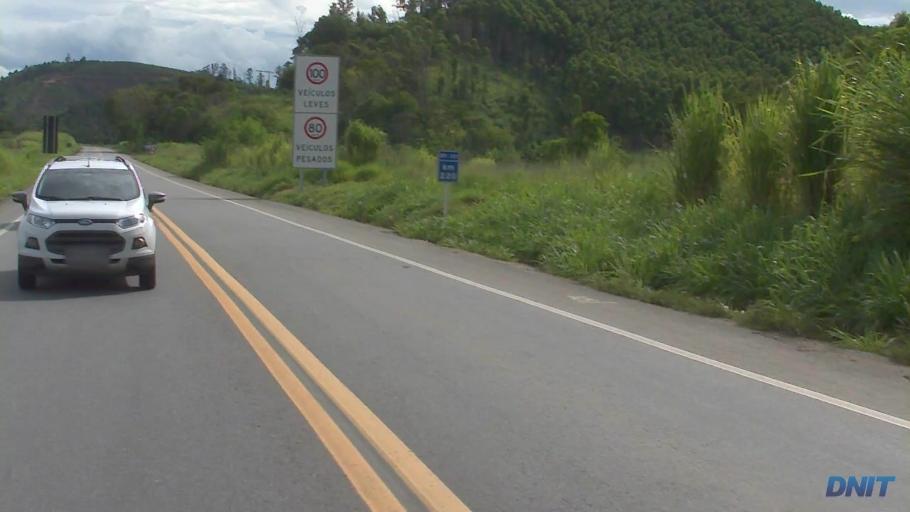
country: BR
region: Minas Gerais
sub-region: Belo Oriente
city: Belo Oriente
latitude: -19.2690
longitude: -42.3558
